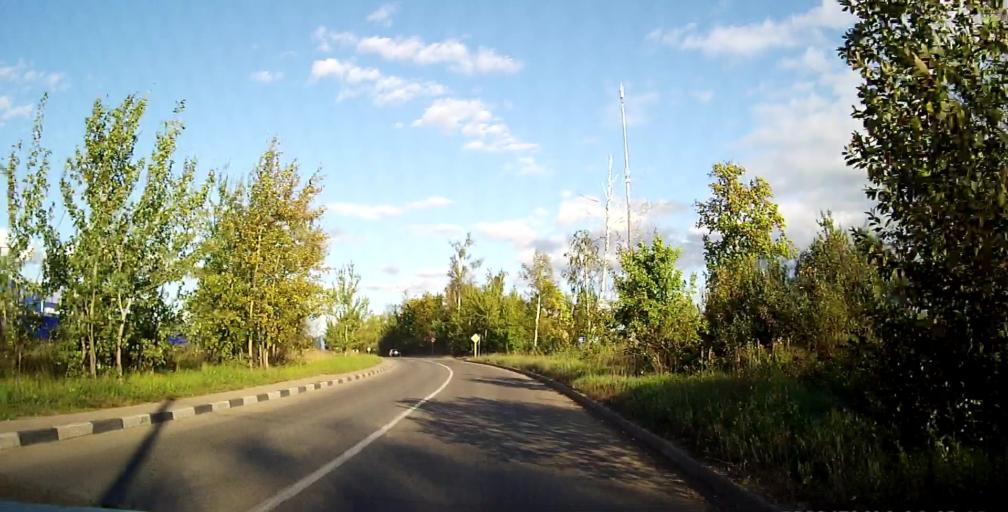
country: RU
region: Moskovskaya
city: Klimovsk
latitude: 55.3613
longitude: 37.5551
